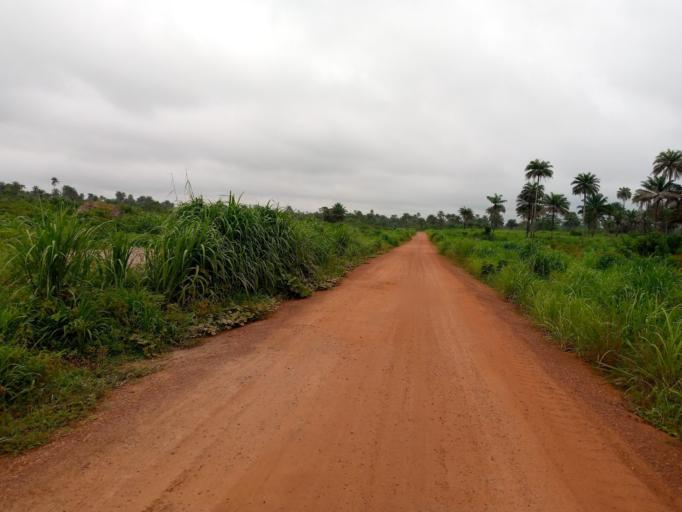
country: SL
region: Southern Province
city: Sumbuya
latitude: 7.5811
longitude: -12.0844
